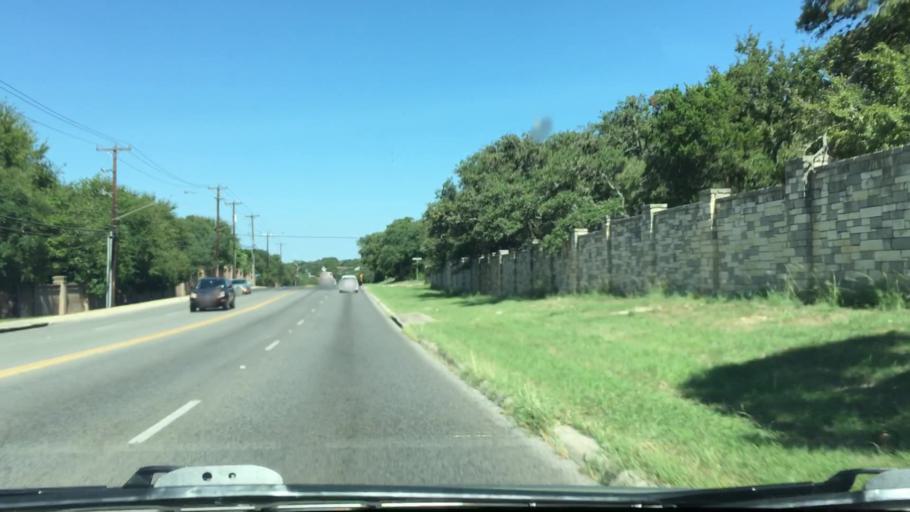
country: US
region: Texas
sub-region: Bexar County
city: Hollywood Park
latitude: 29.5768
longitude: -98.4976
